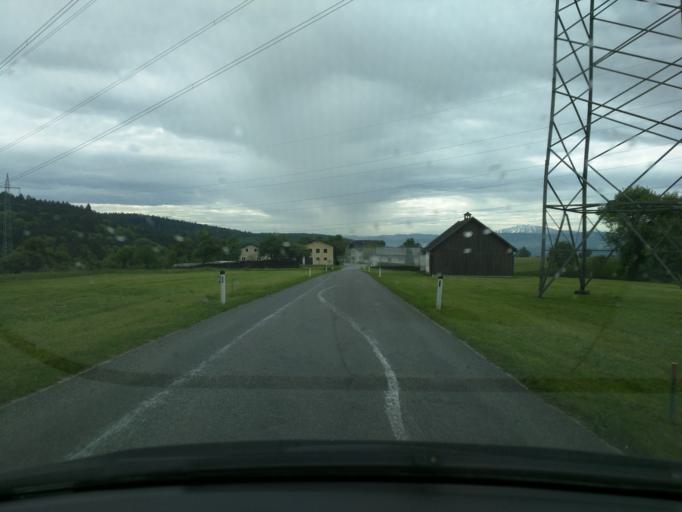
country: AT
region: Lower Austria
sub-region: Politischer Bezirk Melk
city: Blindenmarkt
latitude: 48.1481
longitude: 14.9821
